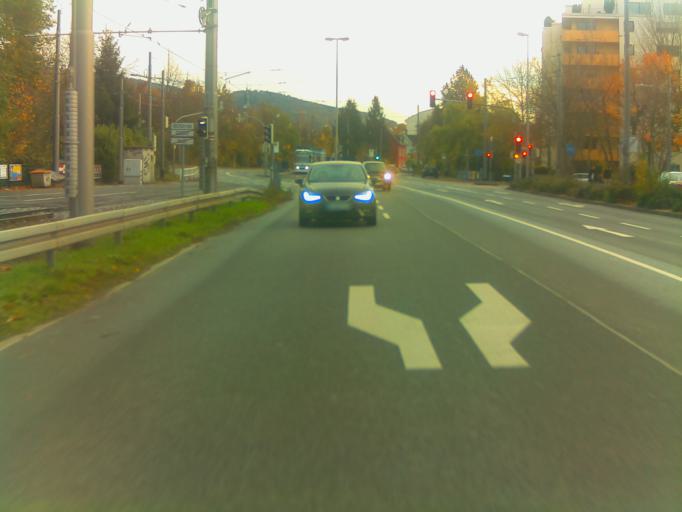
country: DE
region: Baden-Wuerttemberg
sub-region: Karlsruhe Region
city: Dossenheim
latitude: 49.4361
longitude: 8.6813
